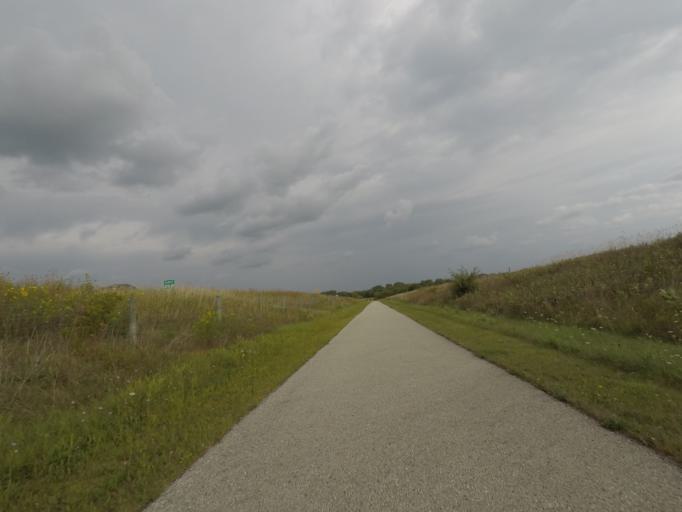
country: US
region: Wisconsin
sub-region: Jefferson County
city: Jefferson
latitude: 42.9735
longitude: -88.8214
